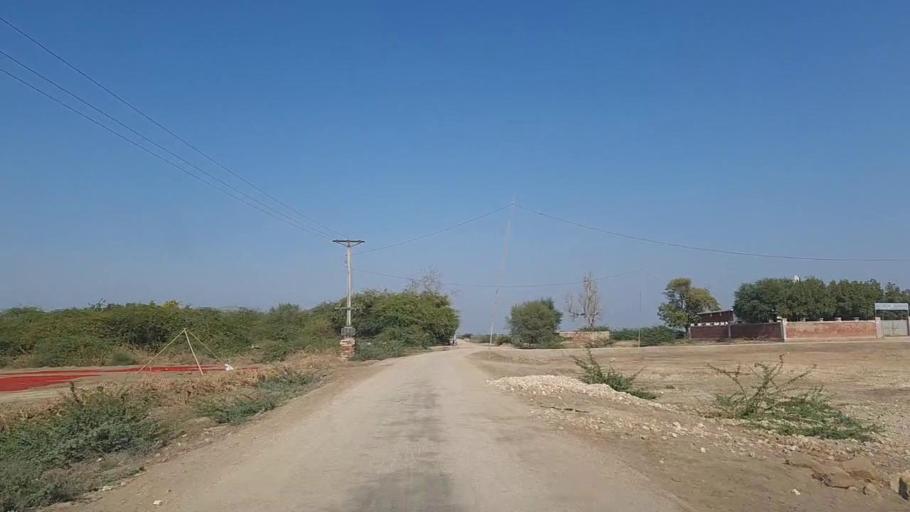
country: PK
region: Sindh
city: Digri
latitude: 25.0931
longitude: 69.2047
